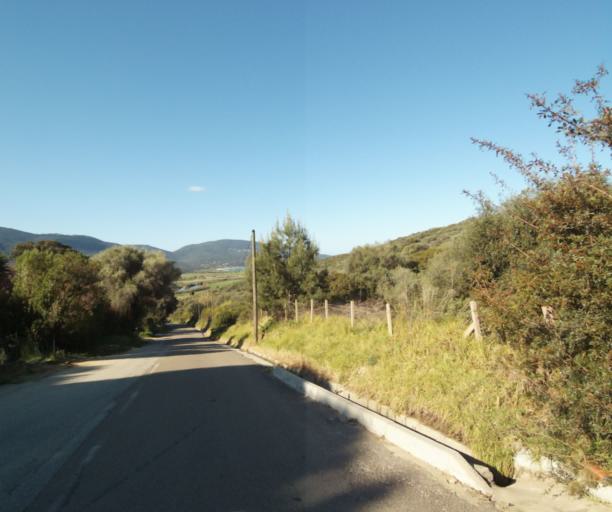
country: FR
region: Corsica
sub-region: Departement de la Corse-du-Sud
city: Propriano
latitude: 41.6689
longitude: 8.8965
